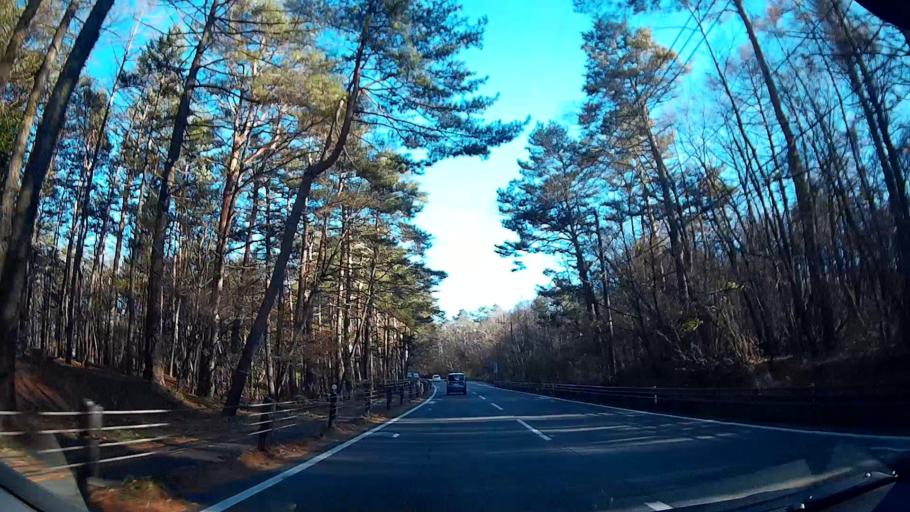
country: JP
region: Yamanashi
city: Fujikawaguchiko
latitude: 35.4513
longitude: 138.8141
